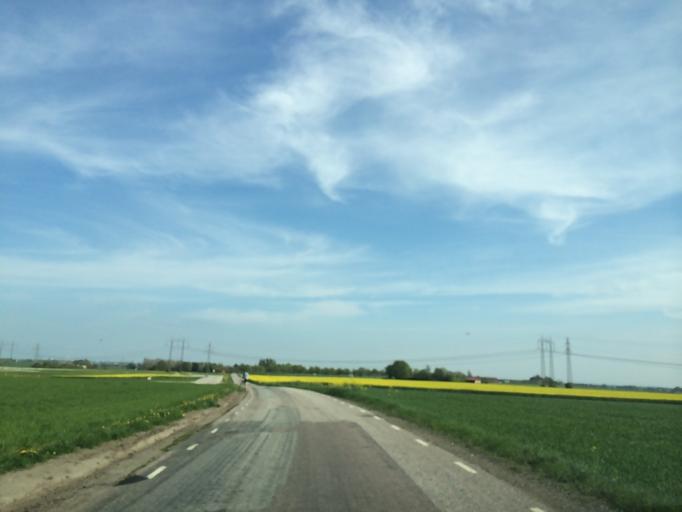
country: SE
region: Skane
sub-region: Kavlinge Kommun
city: Loddekopinge
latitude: 55.7457
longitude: 13.0491
